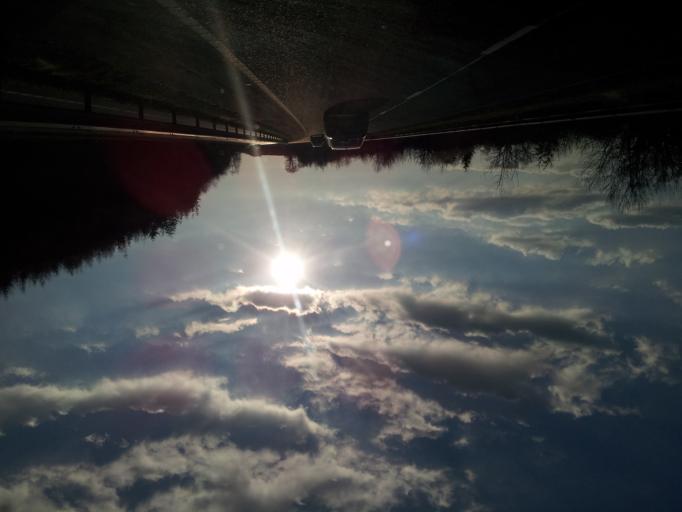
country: GB
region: England
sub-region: Devon
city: Tavistock
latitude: 50.6780
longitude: -4.2151
